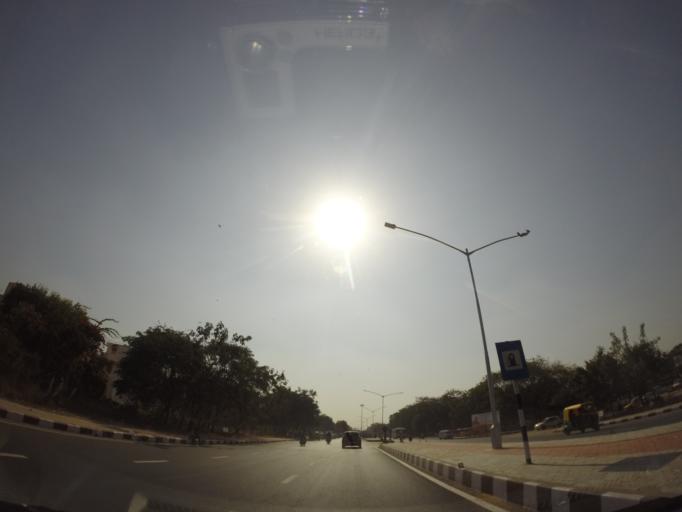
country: IN
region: Gujarat
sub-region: Gandhinagar
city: Ghandinagar
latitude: 23.2095
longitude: 72.6368
